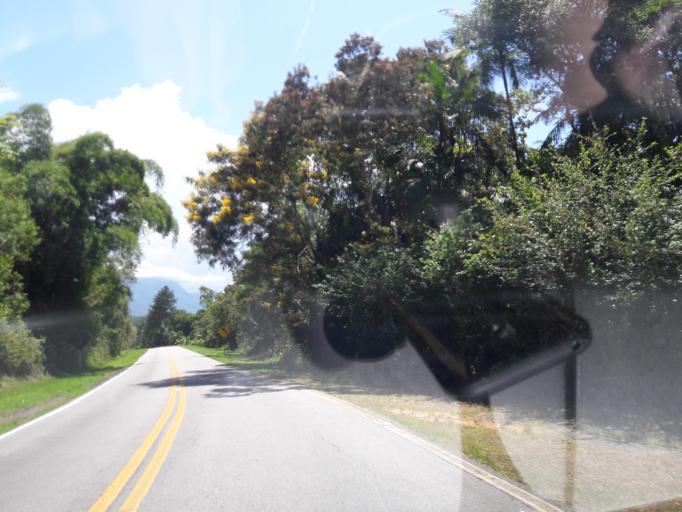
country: BR
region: Parana
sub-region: Antonina
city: Antonina
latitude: -25.5257
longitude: -48.7903
